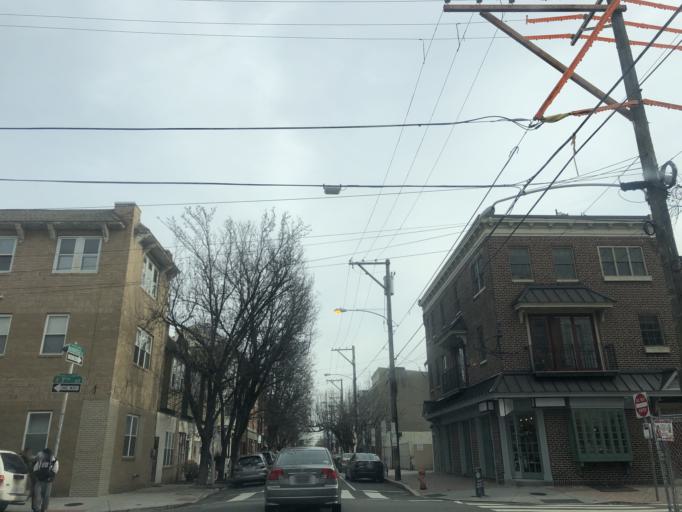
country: US
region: Pennsylvania
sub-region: Philadelphia County
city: Philadelphia
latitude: 39.9413
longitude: -75.1543
